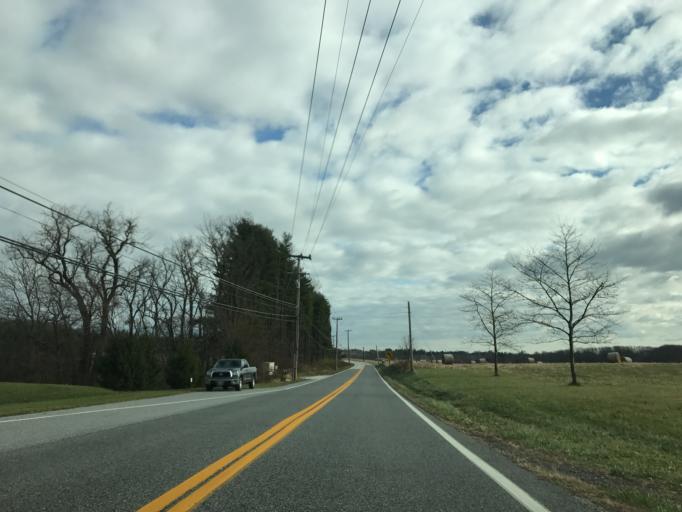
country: US
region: Maryland
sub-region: Harford County
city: Jarrettsville
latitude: 39.5115
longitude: -76.5228
